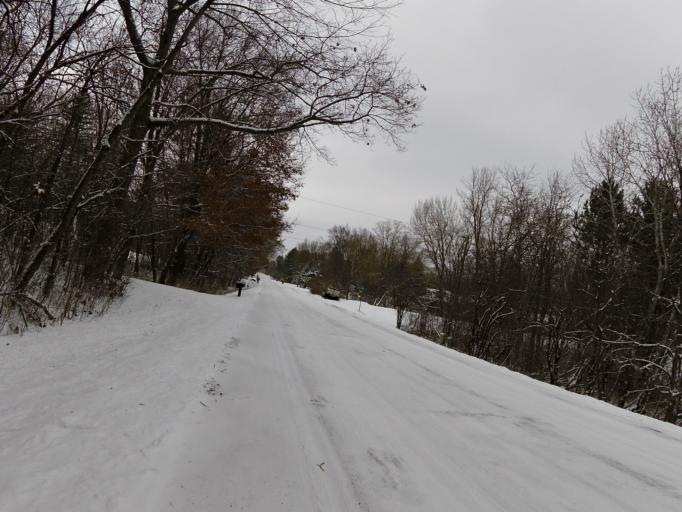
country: US
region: Minnesota
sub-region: Washington County
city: Lake Elmo
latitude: 44.9733
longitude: -92.8377
